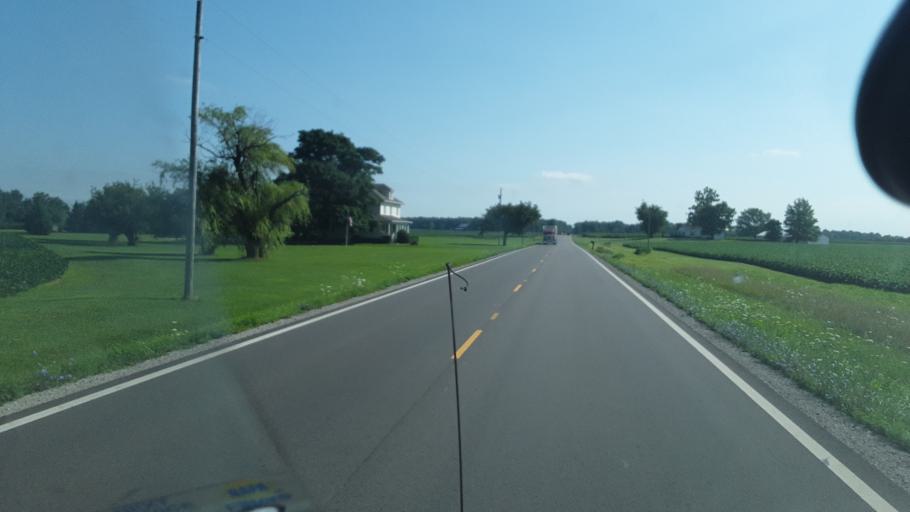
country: US
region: Ohio
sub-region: Marion County
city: Marion
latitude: 40.7013
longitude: -83.0757
